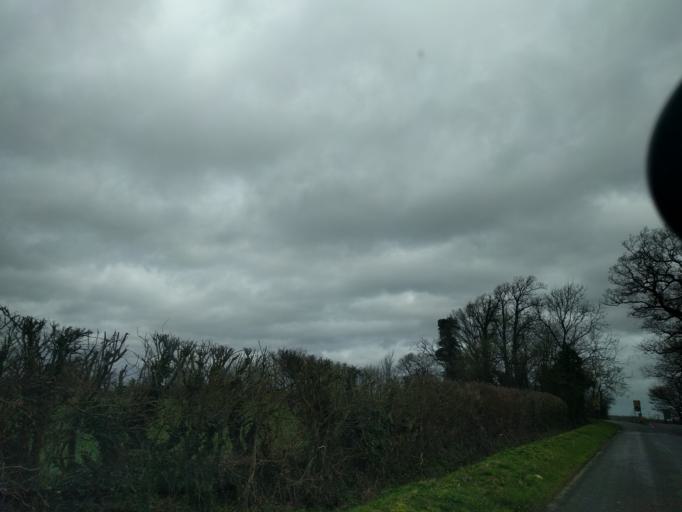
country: GB
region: England
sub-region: Wiltshire
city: Biddestone
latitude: 51.4706
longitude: -2.1956
